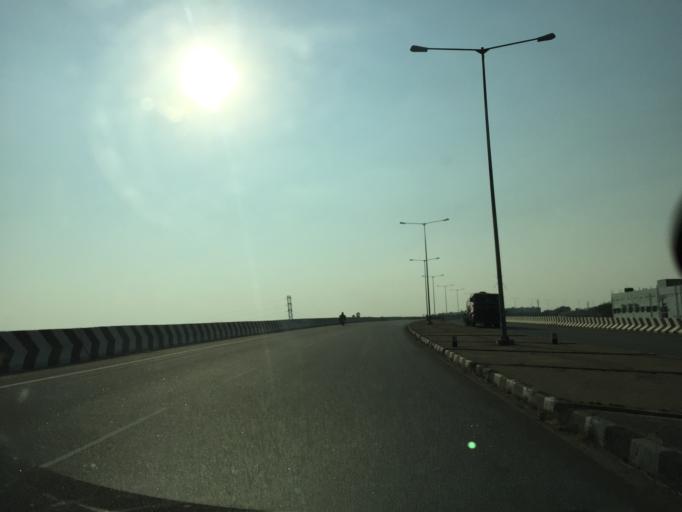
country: IN
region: Telangana
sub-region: Nalgonda
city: Bhongir
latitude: 17.5003
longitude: 78.8920
